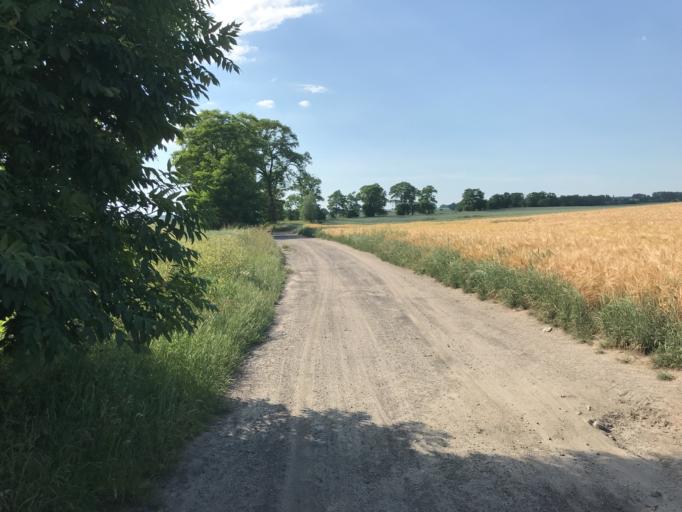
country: PL
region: West Pomeranian Voivodeship
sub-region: Powiat mysliborski
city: Boleszkowice
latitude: 52.7444
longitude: 14.5560
